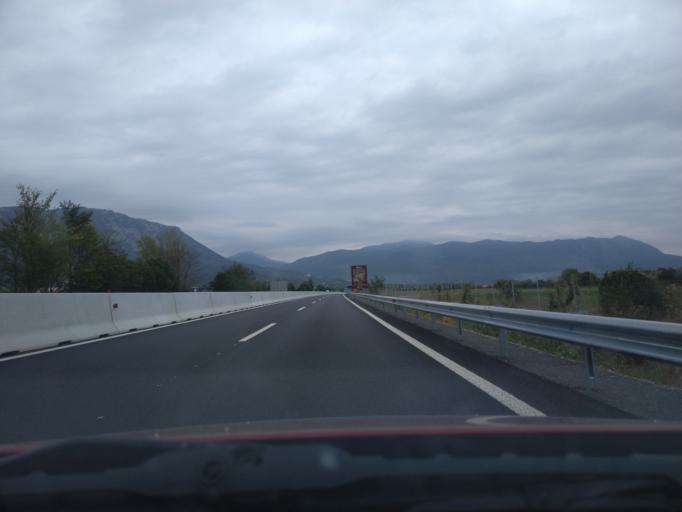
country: SI
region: Ajdovscina
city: Lokavec
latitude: 45.8833
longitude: 13.8879
